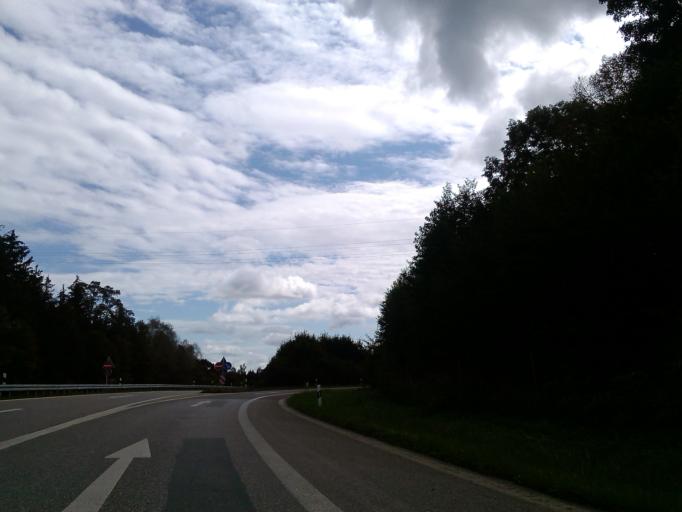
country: DE
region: Bavaria
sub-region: Upper Bavaria
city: Germering
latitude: 48.1186
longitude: 11.3861
